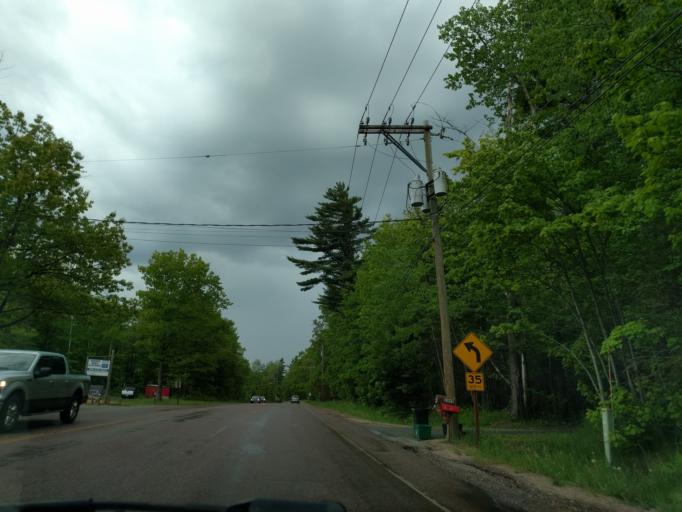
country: US
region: Michigan
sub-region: Marquette County
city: Trowbridge Park
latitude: 46.5608
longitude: -87.4546
